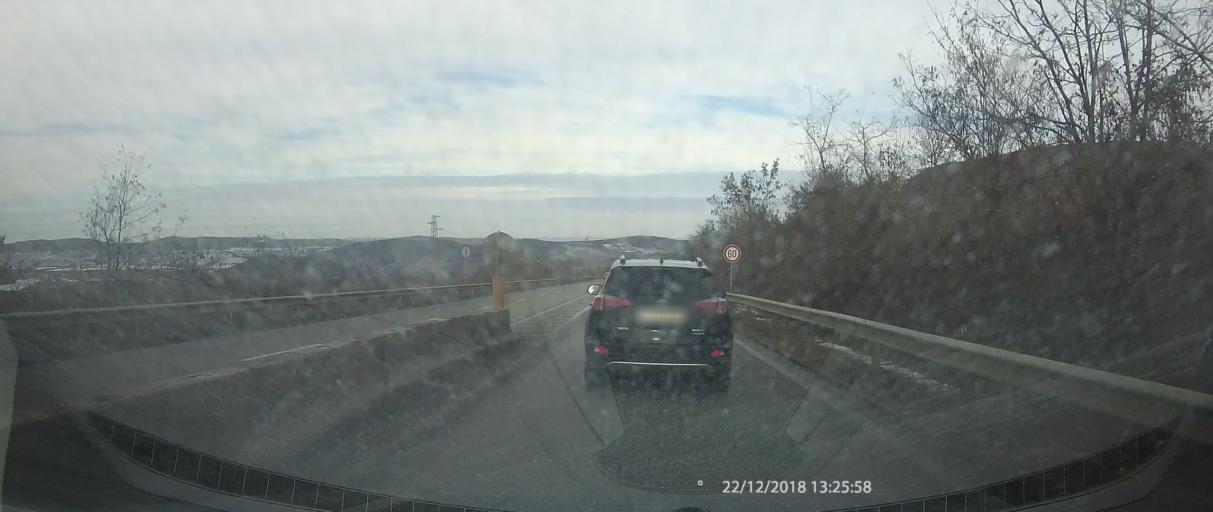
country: BG
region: Lovech
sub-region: Obshtina Yablanitsa
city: Yablanitsa
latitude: 43.0390
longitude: 24.1208
